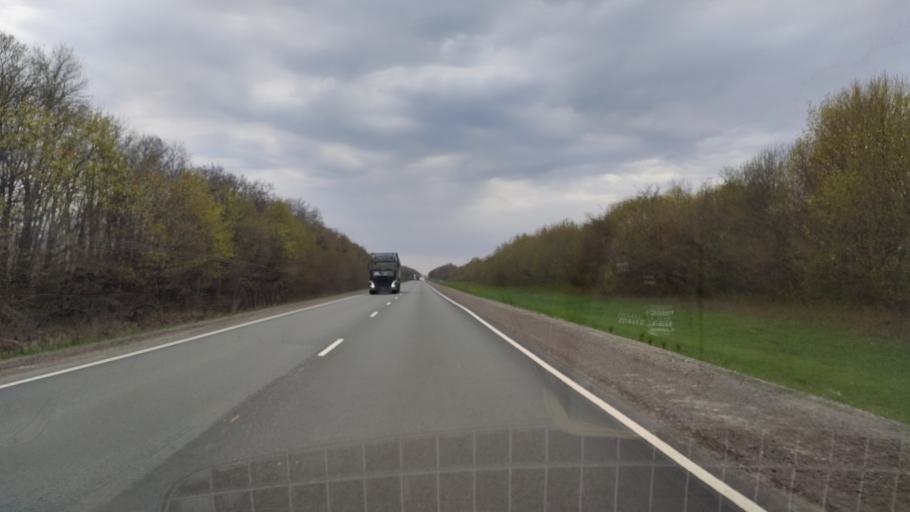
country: RU
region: Voronezj
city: Latnaya
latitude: 51.6294
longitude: 38.6576
